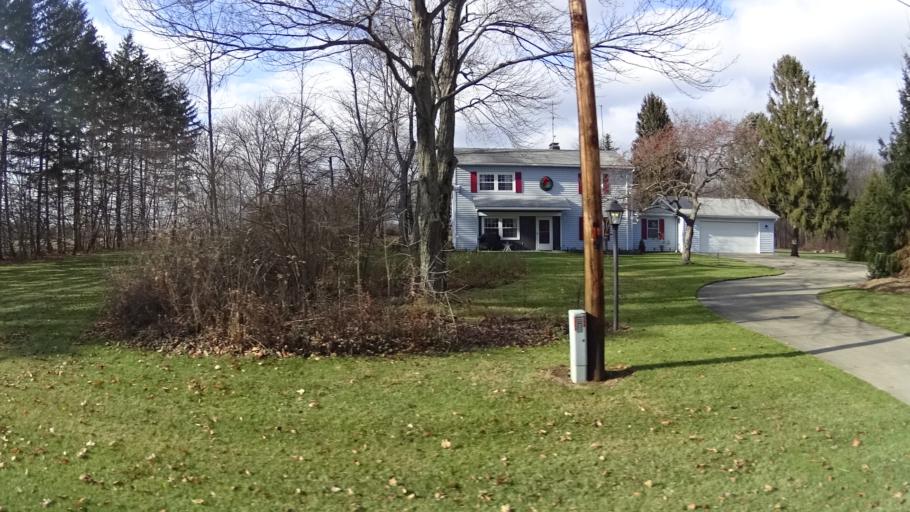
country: US
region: Ohio
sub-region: Lorain County
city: Camden
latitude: 41.2798
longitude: -82.2885
